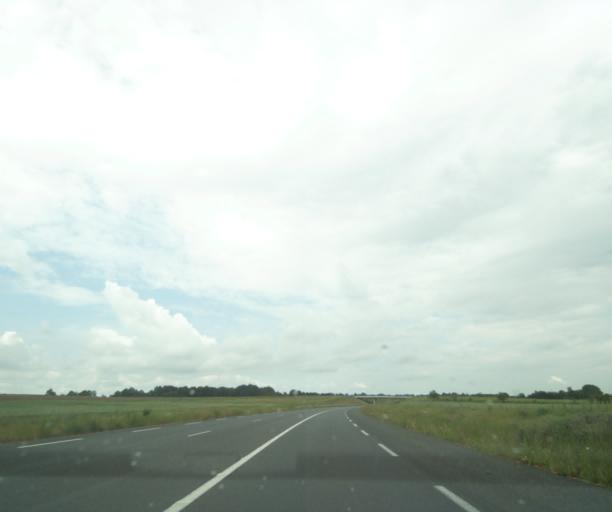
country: FR
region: Poitou-Charentes
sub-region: Departement des Deux-Sevres
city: Louzy
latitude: 47.0529
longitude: -0.1960
